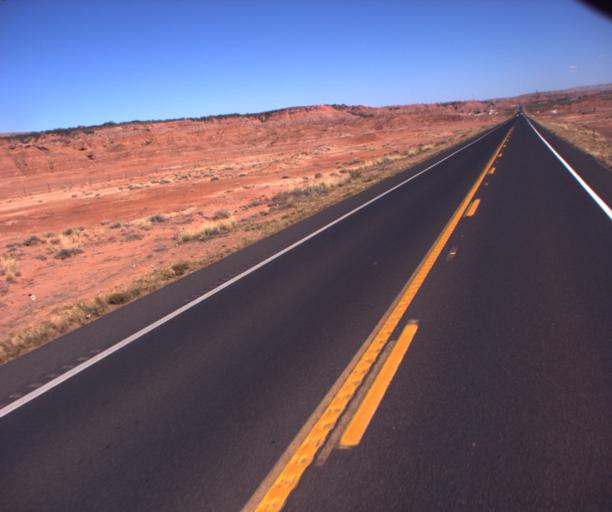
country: US
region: Arizona
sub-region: Coconino County
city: Tuba City
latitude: 36.1032
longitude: -111.2846
